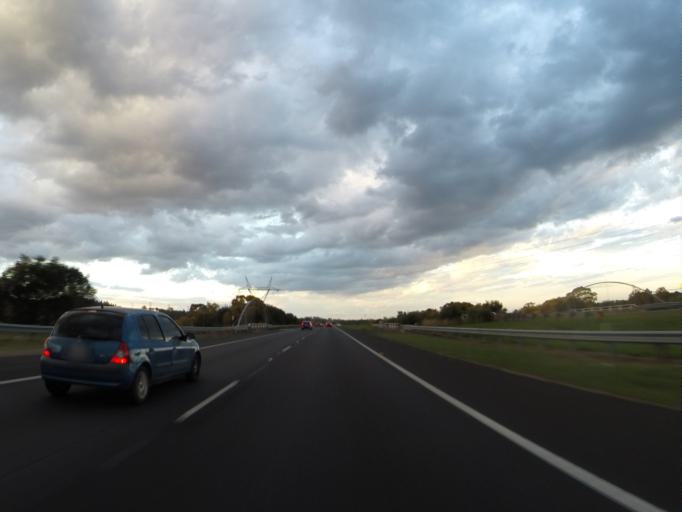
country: AU
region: New South Wales
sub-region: Campbelltown Municipality
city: Glen Alpine
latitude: -34.0868
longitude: 150.7688
